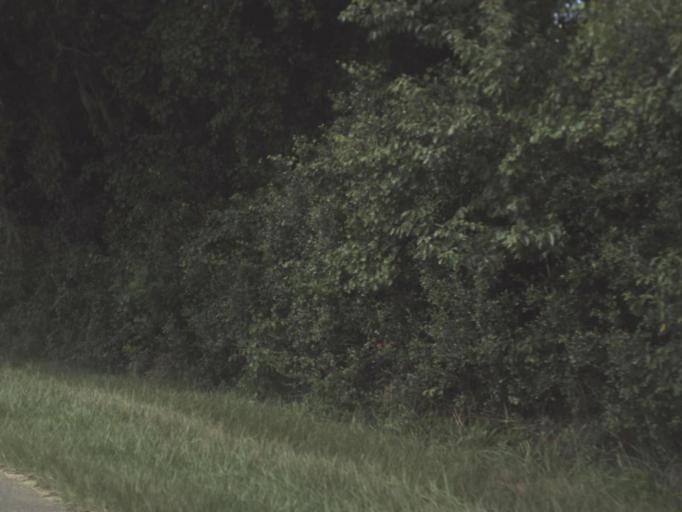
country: US
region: Florida
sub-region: Madison County
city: Madison
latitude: 30.4506
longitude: -83.6274
